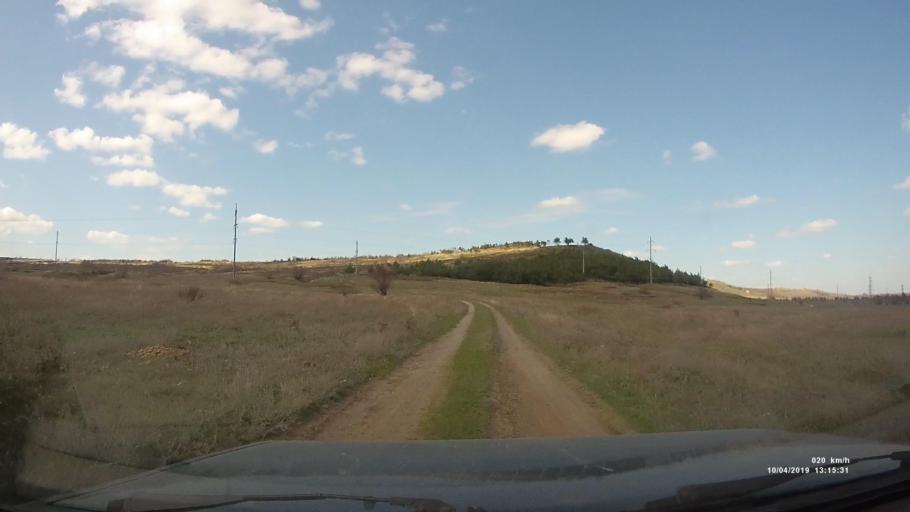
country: RU
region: Rostov
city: Masalovka
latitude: 48.4176
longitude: 40.2589
